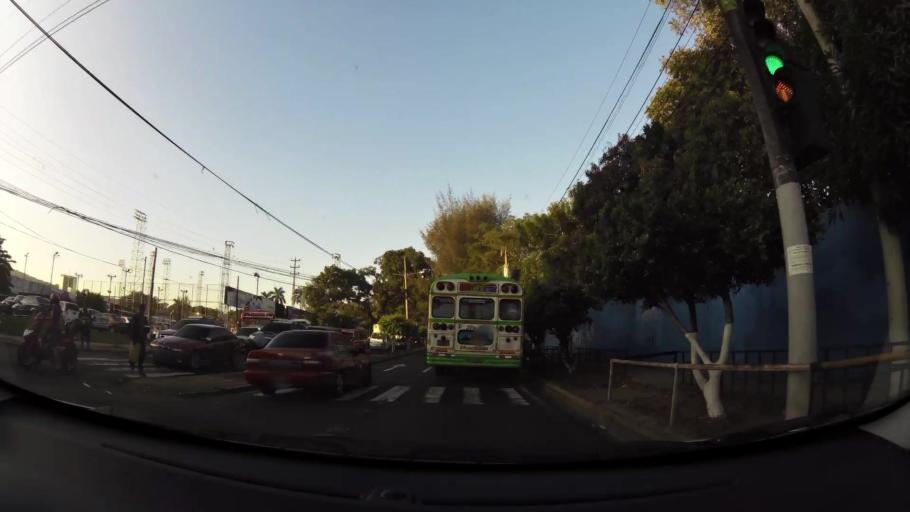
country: SV
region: La Libertad
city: Antiguo Cuscatlan
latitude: 13.6899
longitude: -89.2322
